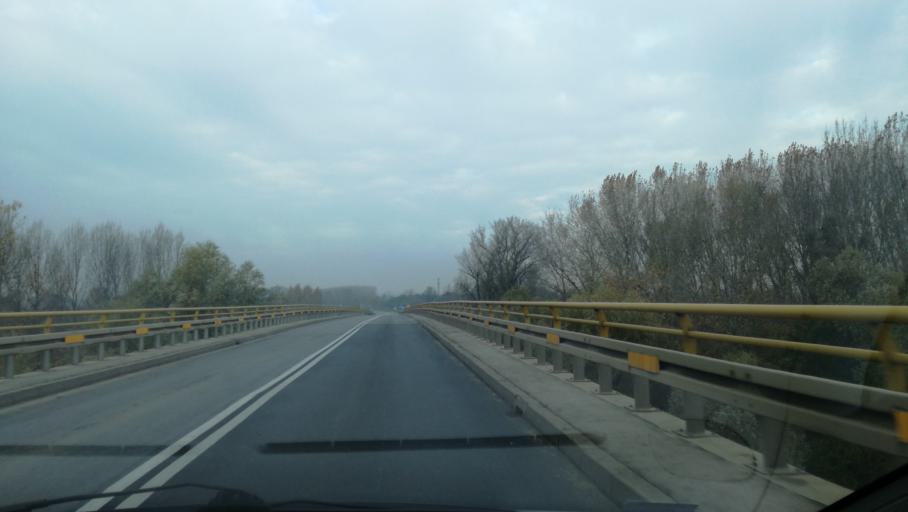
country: RS
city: Taras
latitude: 45.3979
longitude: 20.2116
